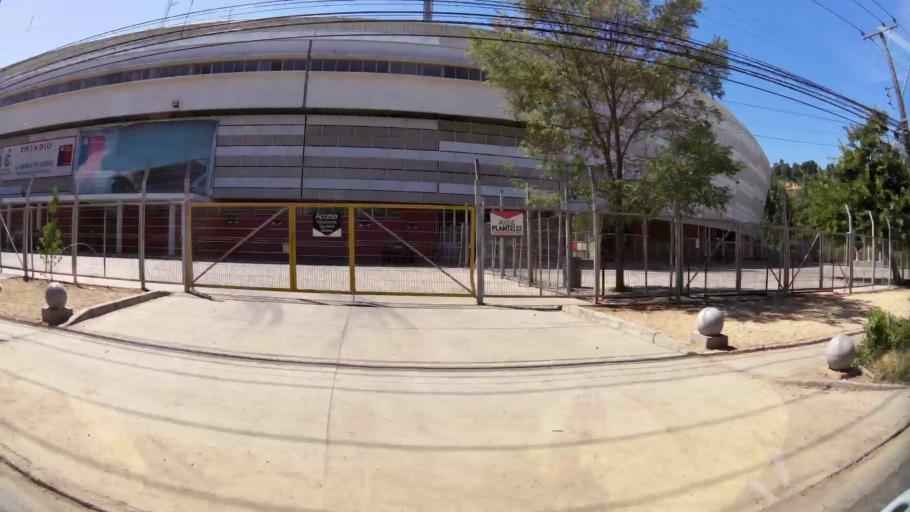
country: CL
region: Maule
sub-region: Provincia de Curico
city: Curico
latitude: -34.9744
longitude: -71.2317
